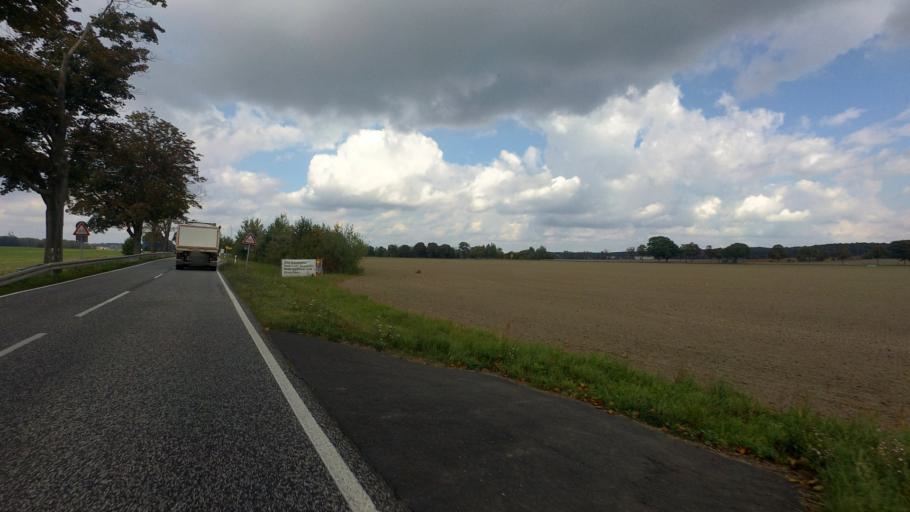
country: DE
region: Brandenburg
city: Juterbog
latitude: 51.9727
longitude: 13.1049
